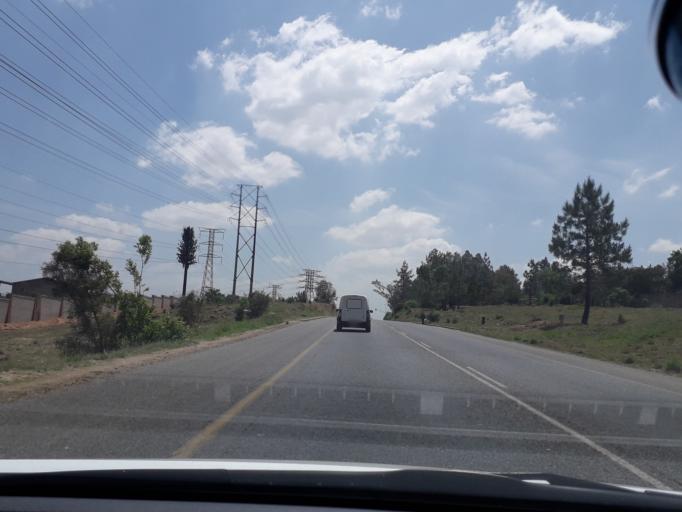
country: ZA
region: Gauteng
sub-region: City of Johannesburg Metropolitan Municipality
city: Midrand
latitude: -26.0064
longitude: 28.0958
